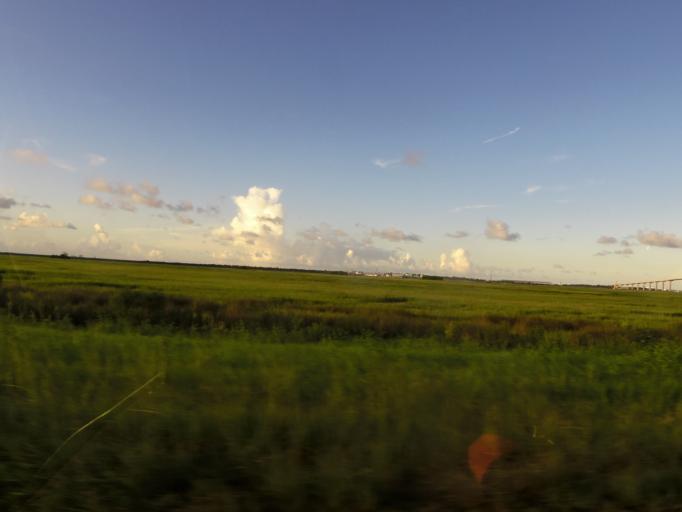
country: US
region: Georgia
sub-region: Glynn County
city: Brunswick
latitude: 31.1067
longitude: -81.5036
